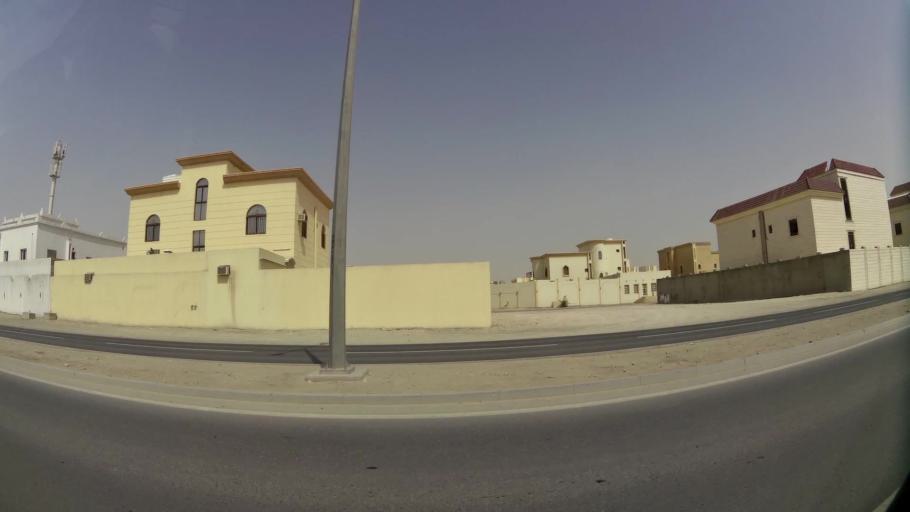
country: QA
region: Baladiyat ar Rayyan
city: Ar Rayyan
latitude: 25.2358
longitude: 51.3825
